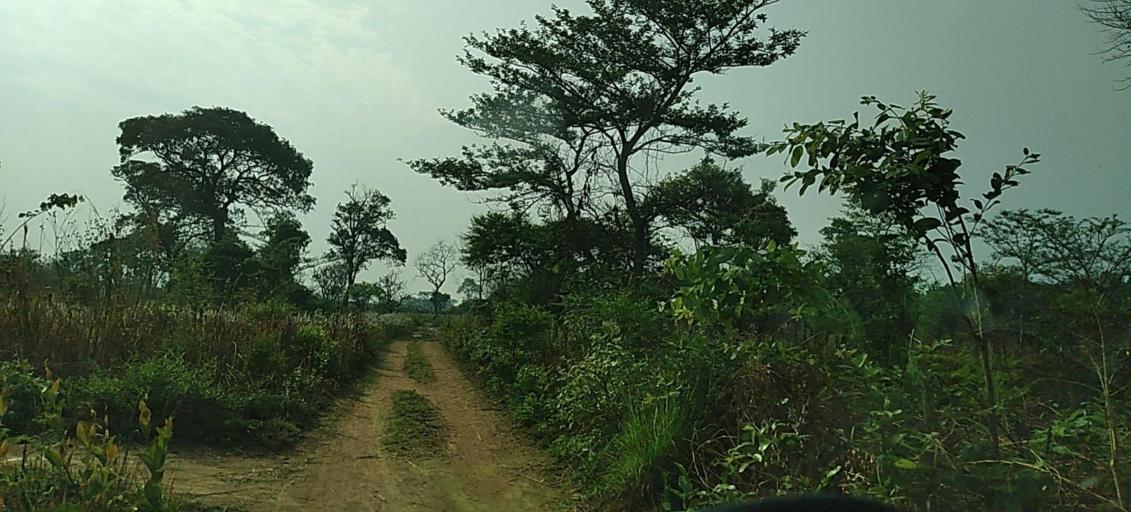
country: ZM
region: North-Western
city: Solwezi
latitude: -12.3862
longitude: 26.5682
